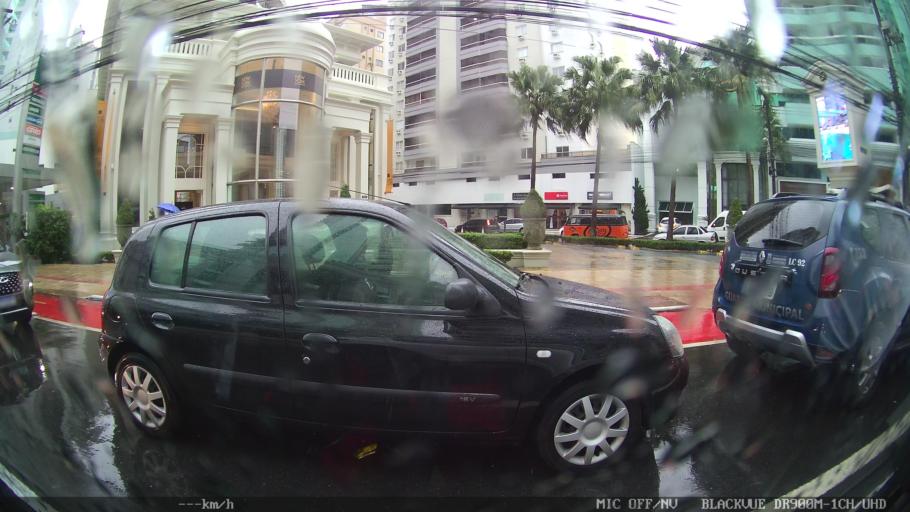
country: BR
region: Santa Catarina
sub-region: Balneario Camboriu
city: Balneario Camboriu
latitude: -26.9998
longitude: -48.6244
